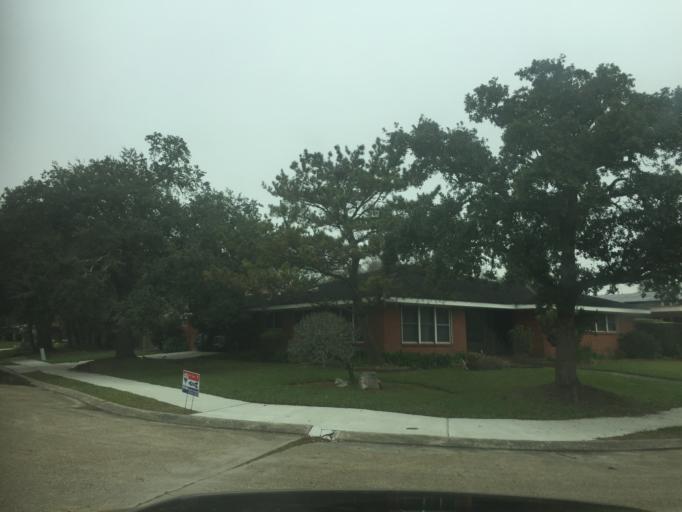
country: US
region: Louisiana
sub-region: Jefferson Parish
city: Metairie
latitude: 30.0207
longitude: -90.0996
